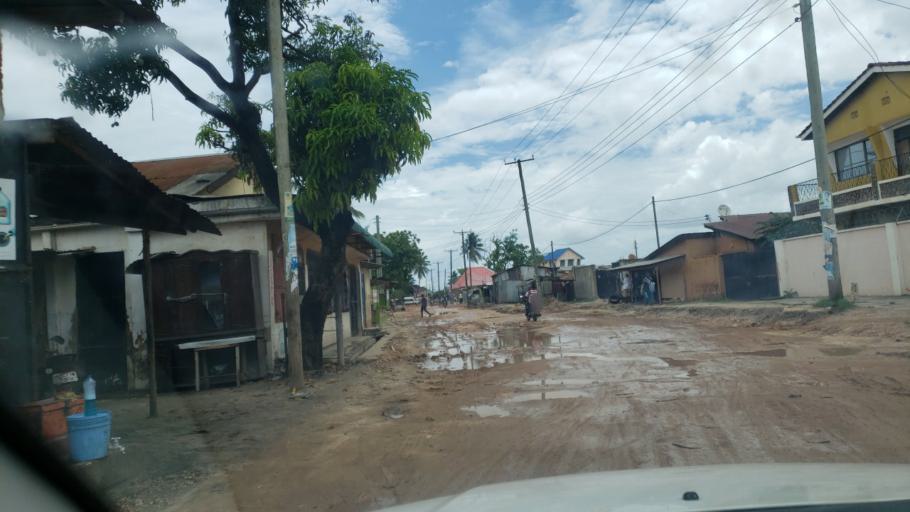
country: TZ
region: Dar es Salaam
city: Magomeni
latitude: -6.8068
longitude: 39.2308
